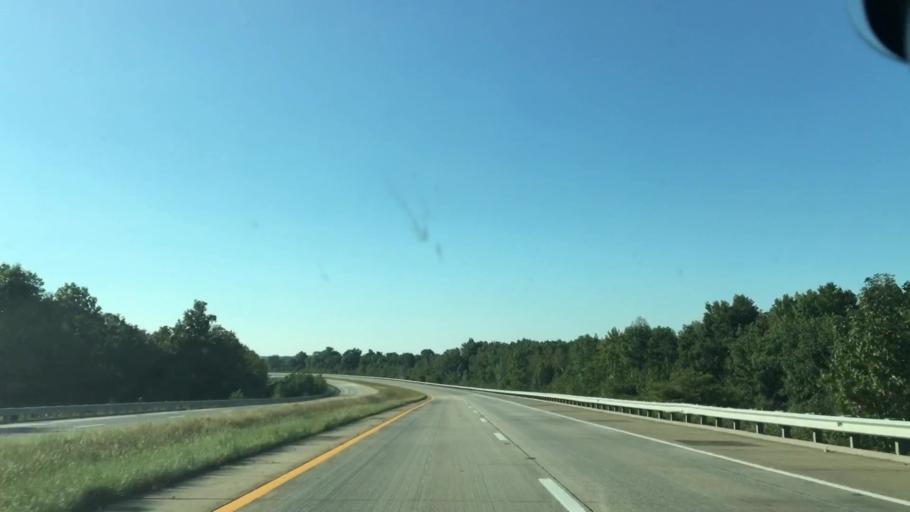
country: US
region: Kentucky
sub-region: Daviess County
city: Owensboro
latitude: 37.7586
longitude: -87.2993
